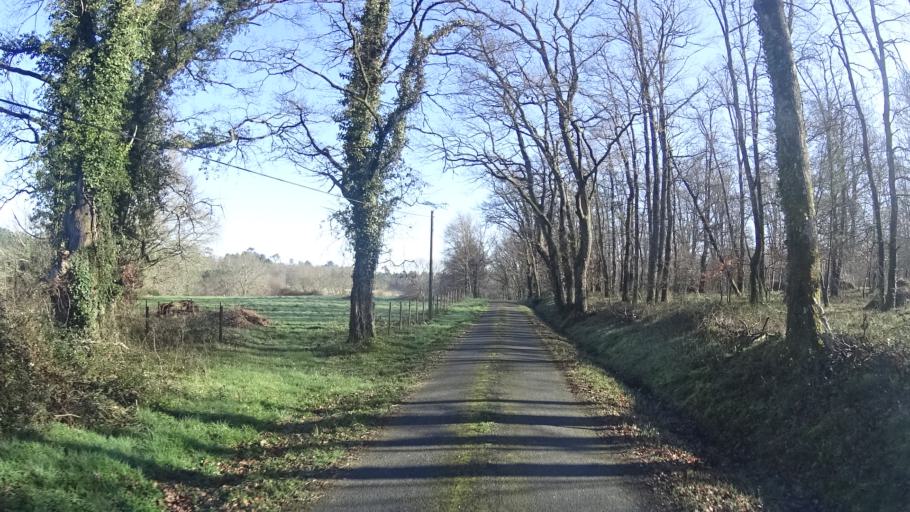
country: FR
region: Aquitaine
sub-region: Departement de la Dordogne
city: La Roche-Chalais
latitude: 45.1573
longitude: 0.0166
